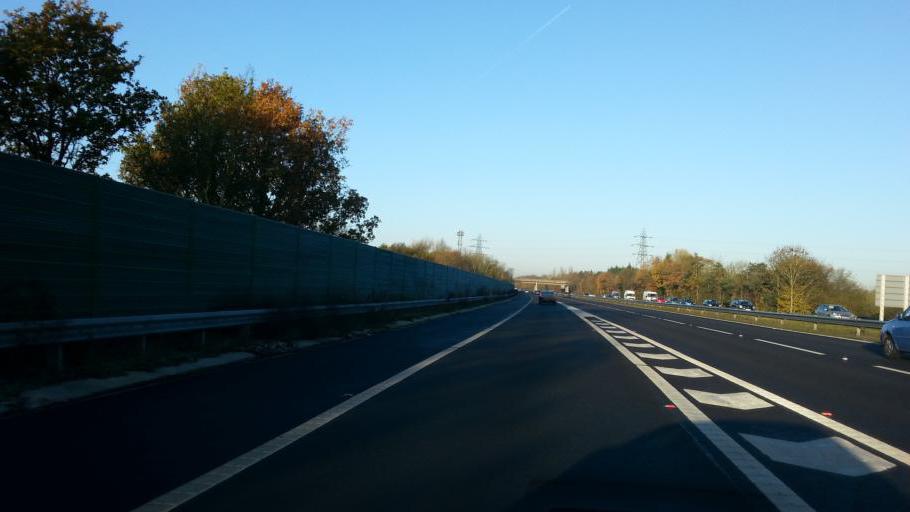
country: GB
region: England
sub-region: Wokingham
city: Winnersh
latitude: 51.4359
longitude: -0.8668
